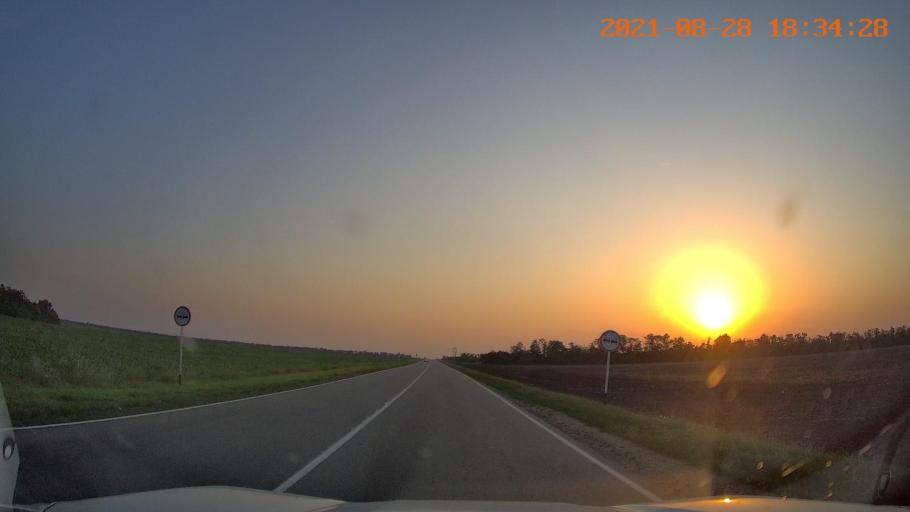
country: RU
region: Adygeya
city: Giaginskaya
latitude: 44.8790
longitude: 40.1547
